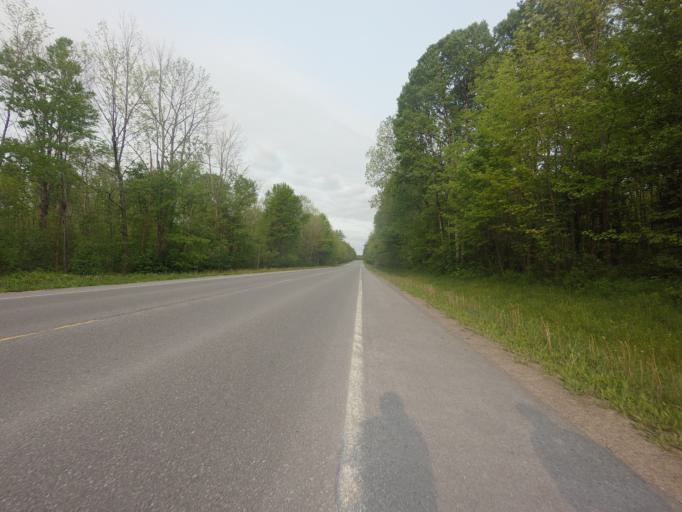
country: US
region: New York
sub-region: Jefferson County
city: Carthage
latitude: 44.0336
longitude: -75.5901
